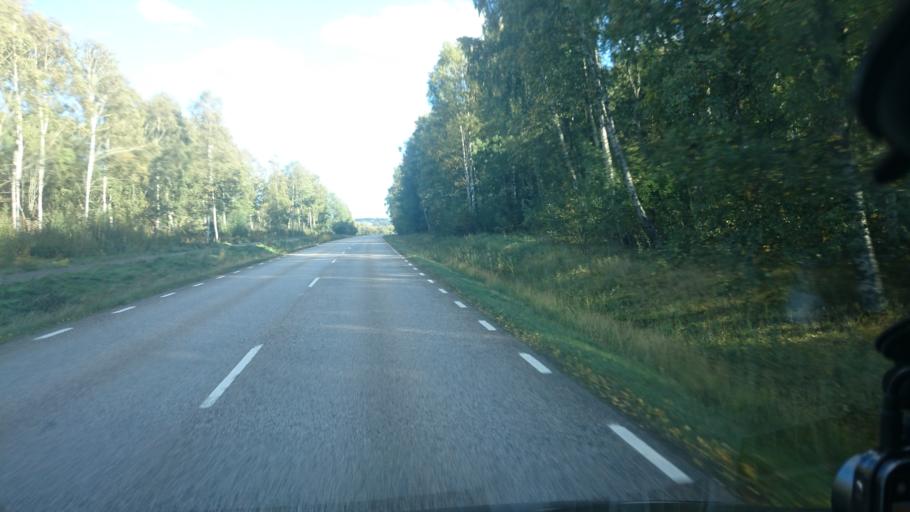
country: SE
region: Vaestra Goetaland
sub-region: Lysekils Kommun
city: Lysekil
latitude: 58.3340
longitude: 11.4409
